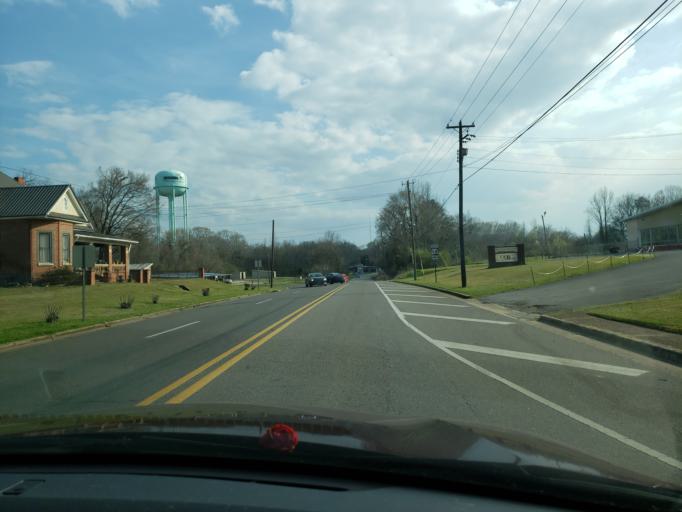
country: US
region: Alabama
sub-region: Hale County
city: Greensboro
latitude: 32.7022
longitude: -87.6069
